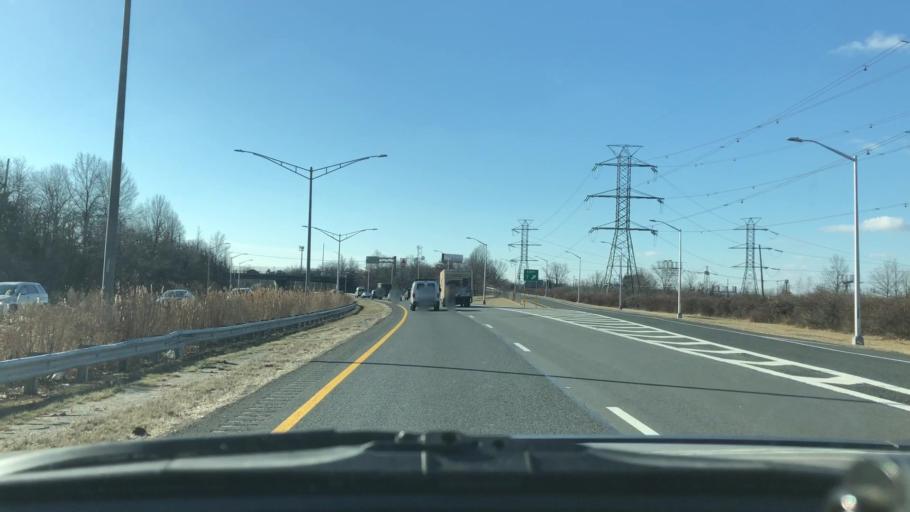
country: US
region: New York
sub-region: Richmond County
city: Bloomfield
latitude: 40.5927
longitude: -74.1932
